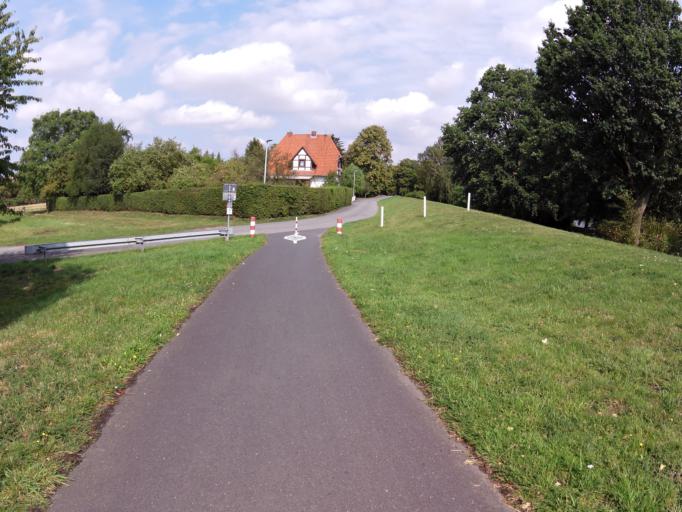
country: DE
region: Lower Saxony
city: Hoya
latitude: 52.8025
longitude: 9.1443
